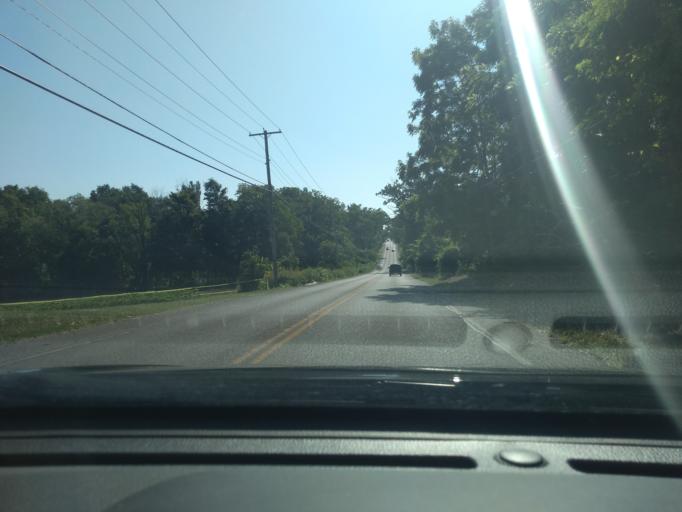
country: US
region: New York
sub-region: Erie County
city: Orchard Park
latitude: 42.7891
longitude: -78.7314
